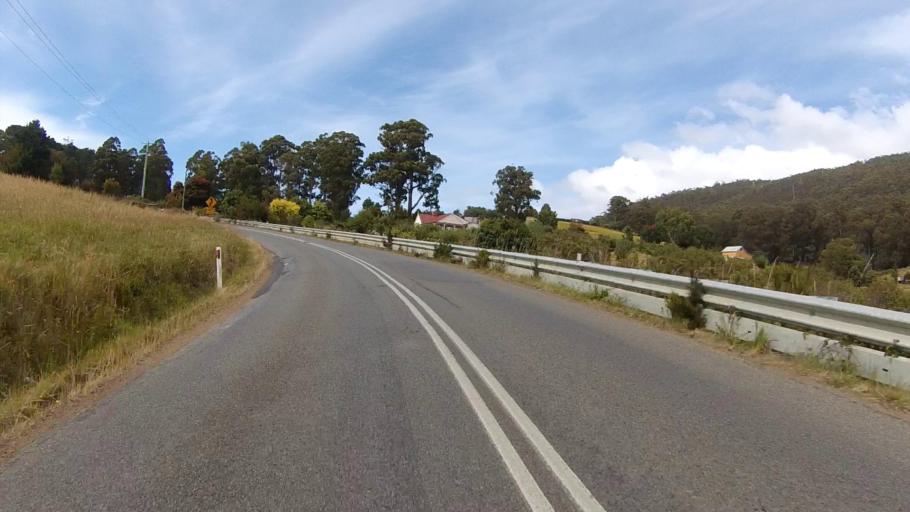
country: AU
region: Tasmania
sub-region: Kingborough
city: Kettering
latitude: -43.1991
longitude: 147.2510
